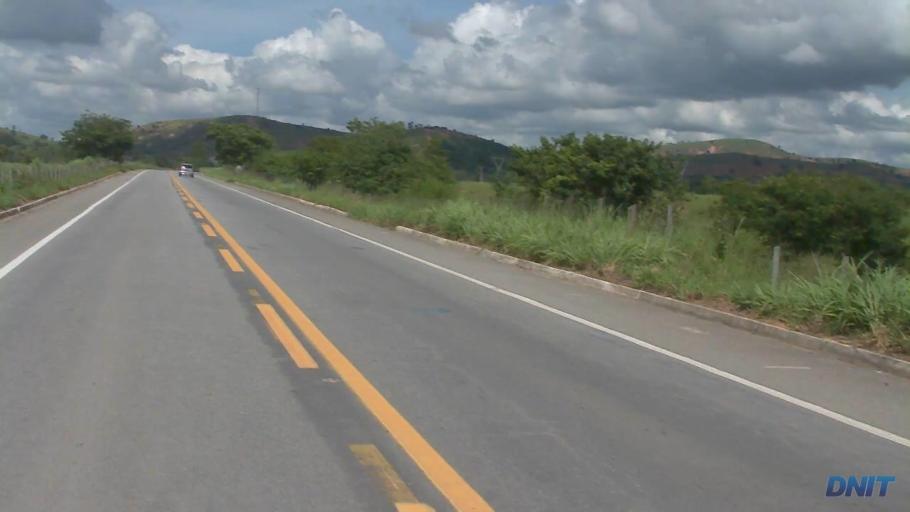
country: BR
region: Minas Gerais
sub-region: Governador Valadares
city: Governador Valadares
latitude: -19.0101
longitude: -42.1369
